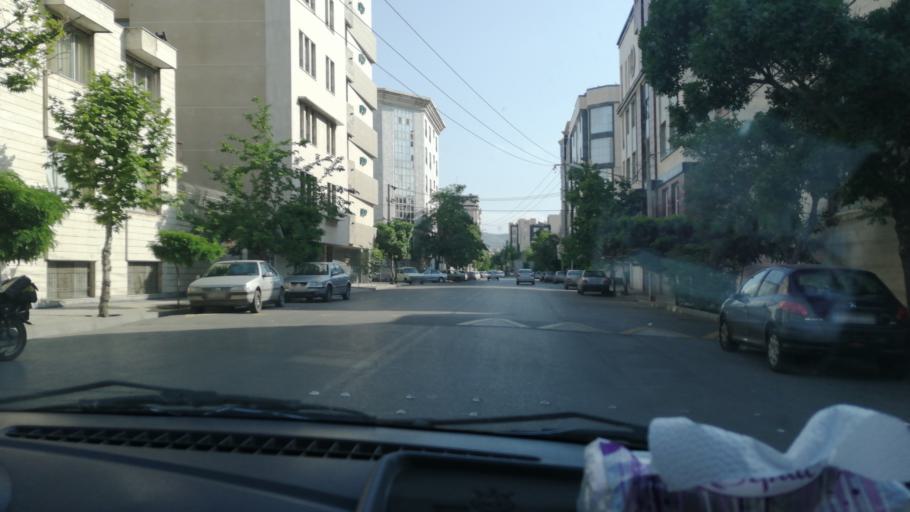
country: IR
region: Razavi Khorasan
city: Mashhad
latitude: 36.3101
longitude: 59.5609
